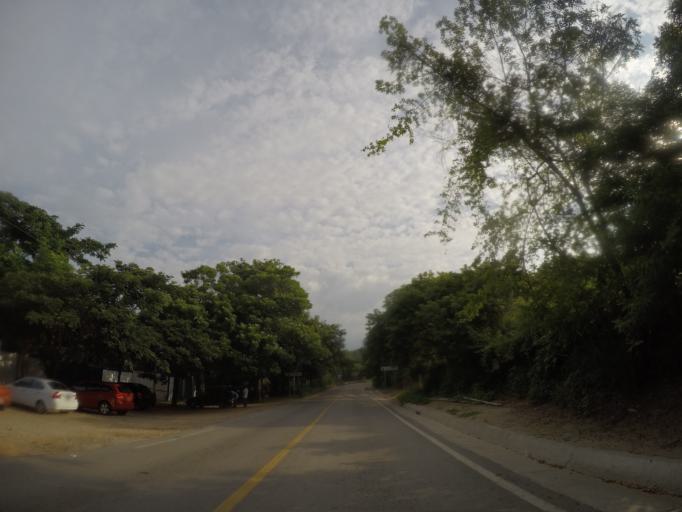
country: MX
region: Oaxaca
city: San Pedro Pochutla
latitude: 15.7114
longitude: -96.4828
